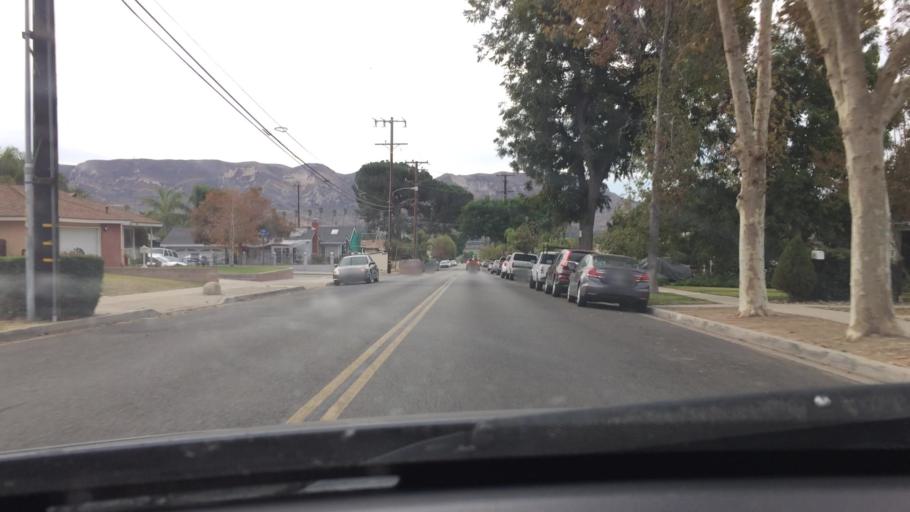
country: US
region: California
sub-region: Ventura County
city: Fillmore
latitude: 34.4027
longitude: -118.9094
